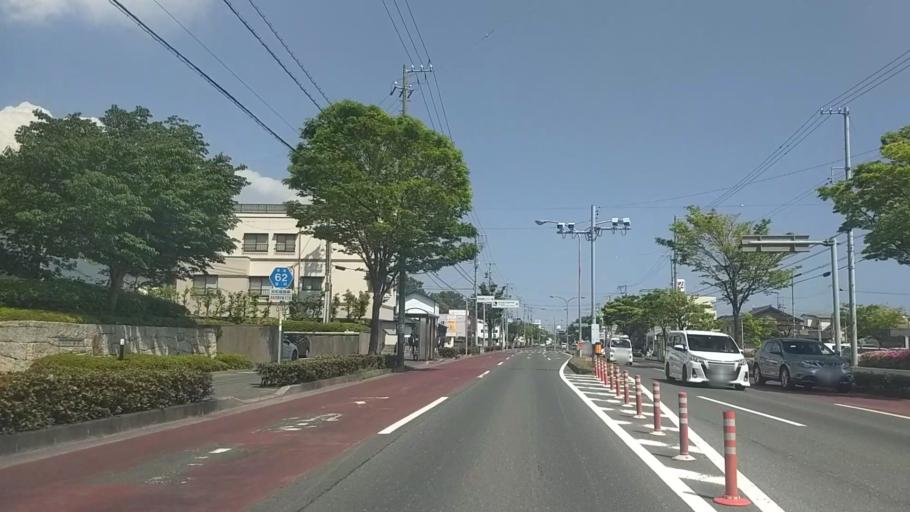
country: JP
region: Shizuoka
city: Hamamatsu
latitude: 34.6997
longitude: 137.7164
